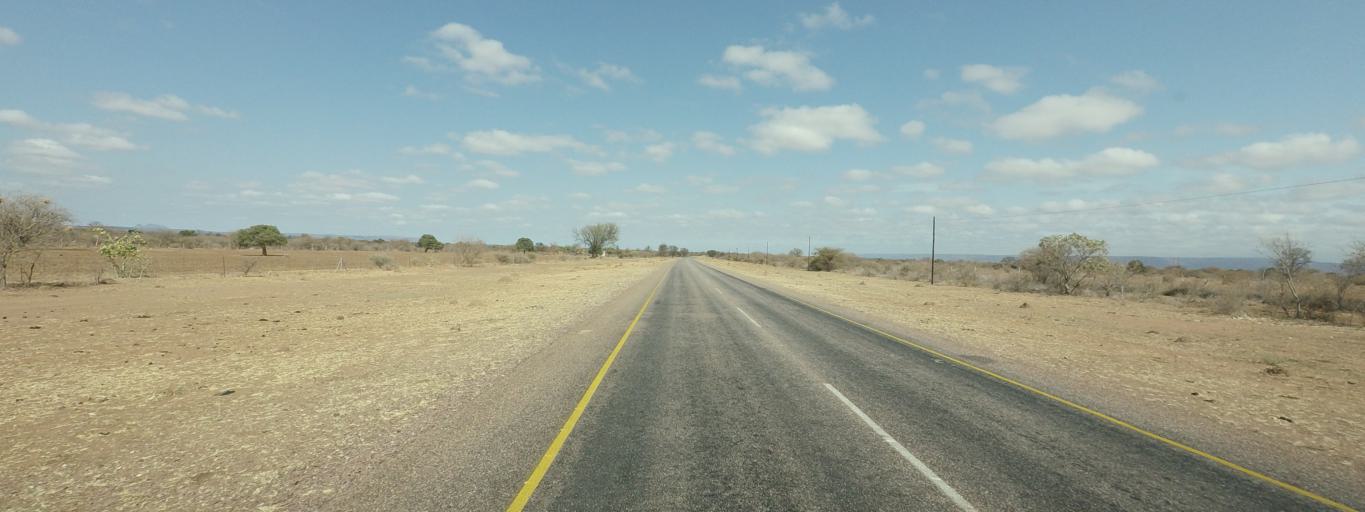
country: BW
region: Central
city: Ratholo
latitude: -22.8141
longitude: 27.5503
